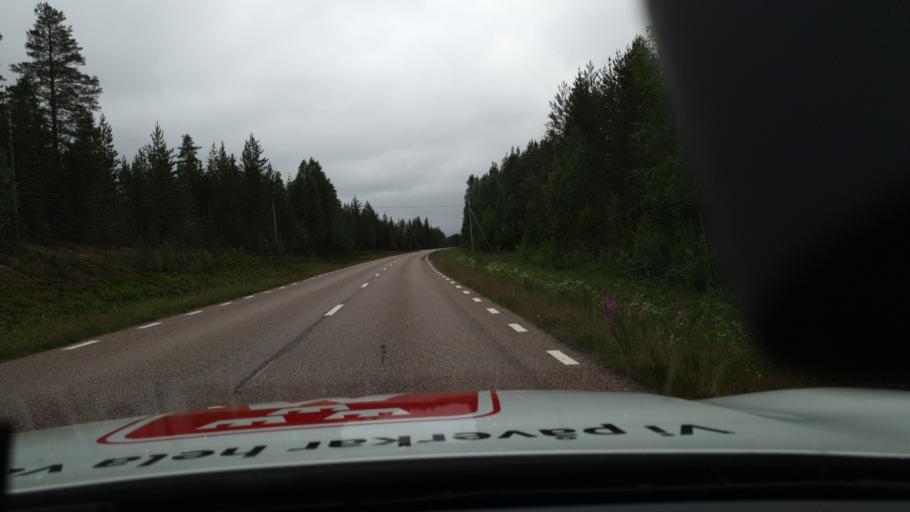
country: FI
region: Lapland
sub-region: Tunturi-Lappi
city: Kolari
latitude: 67.0165
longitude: 23.7316
